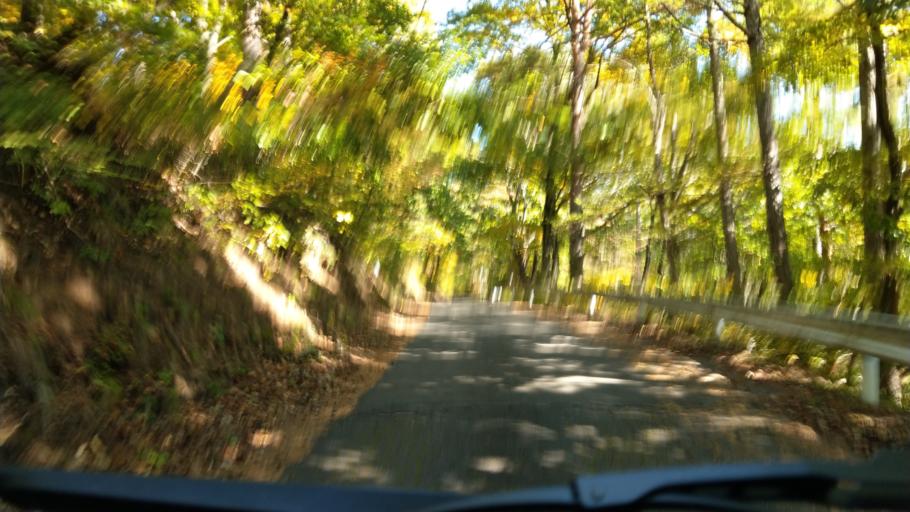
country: JP
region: Nagano
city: Komoro
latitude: 36.3690
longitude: 138.4093
